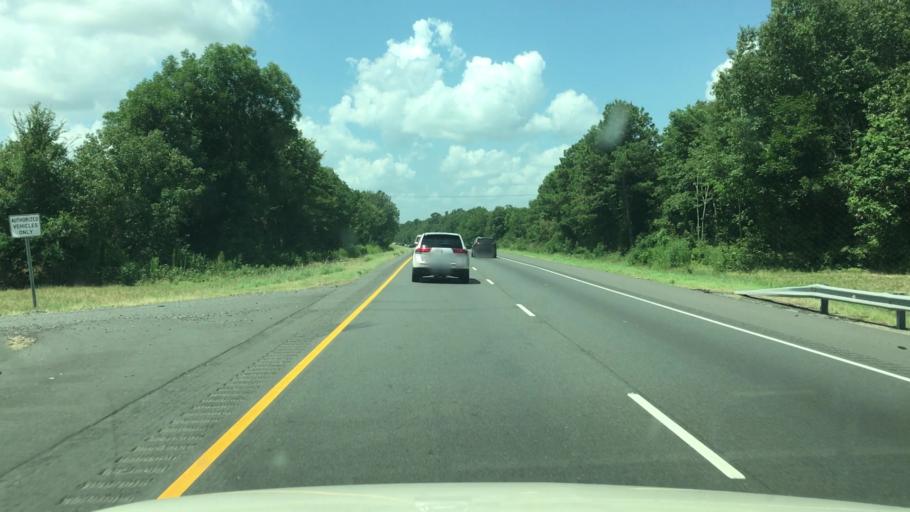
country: US
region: Arkansas
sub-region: Hempstead County
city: Hope
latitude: 33.7214
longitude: -93.5545
